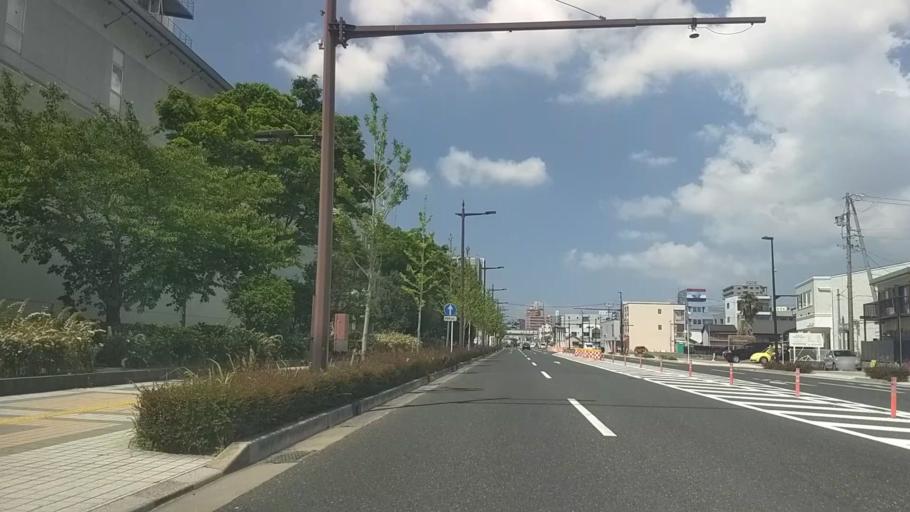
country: JP
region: Shizuoka
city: Hamamatsu
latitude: 34.7132
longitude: 137.7400
